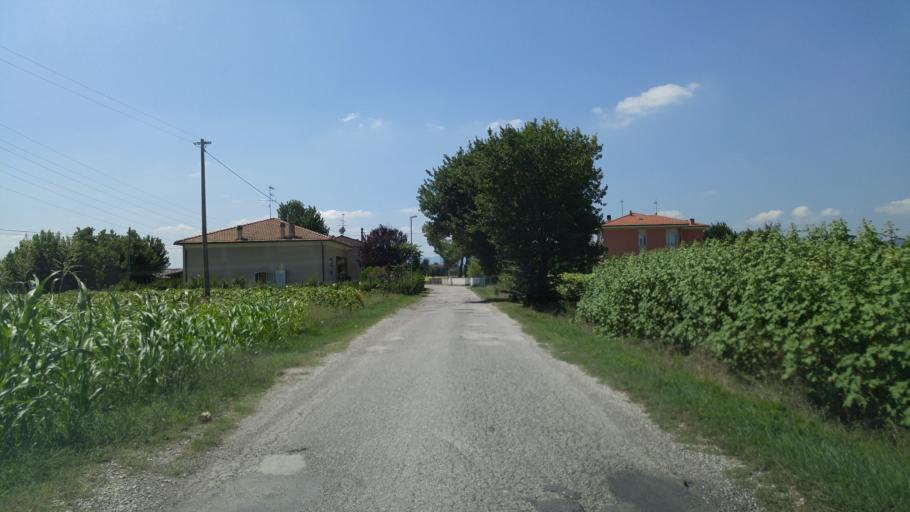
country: IT
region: The Marches
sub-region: Provincia di Pesaro e Urbino
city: Cuccurano
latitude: 43.7931
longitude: 12.9669
